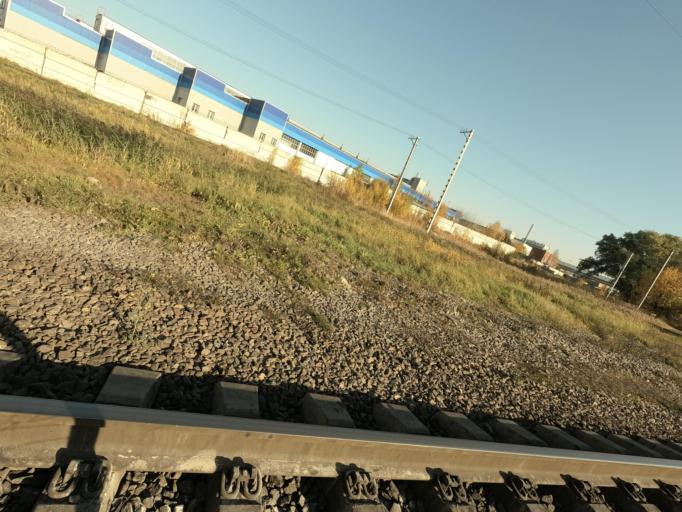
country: RU
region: St.-Petersburg
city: Obukhovo
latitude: 59.8501
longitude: 30.4534
